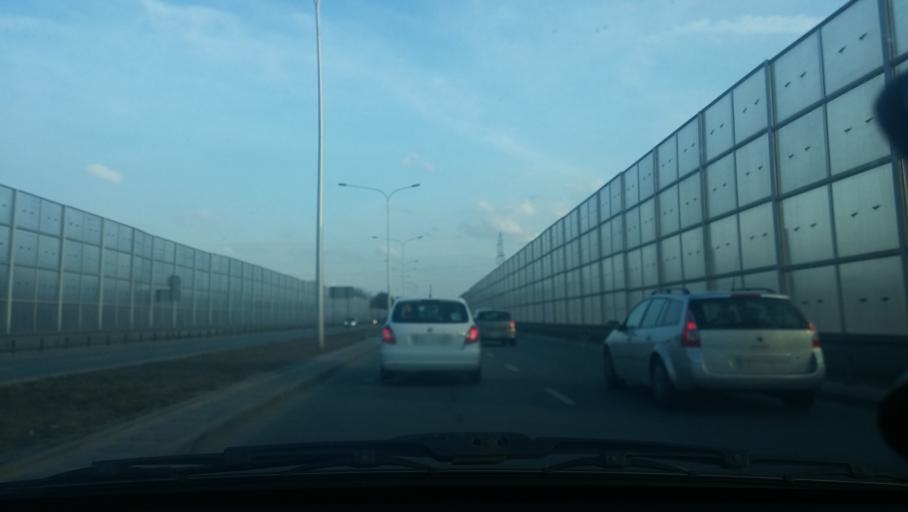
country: PL
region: Masovian Voivodeship
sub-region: Warszawa
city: Ursus
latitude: 52.1968
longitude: 20.9058
